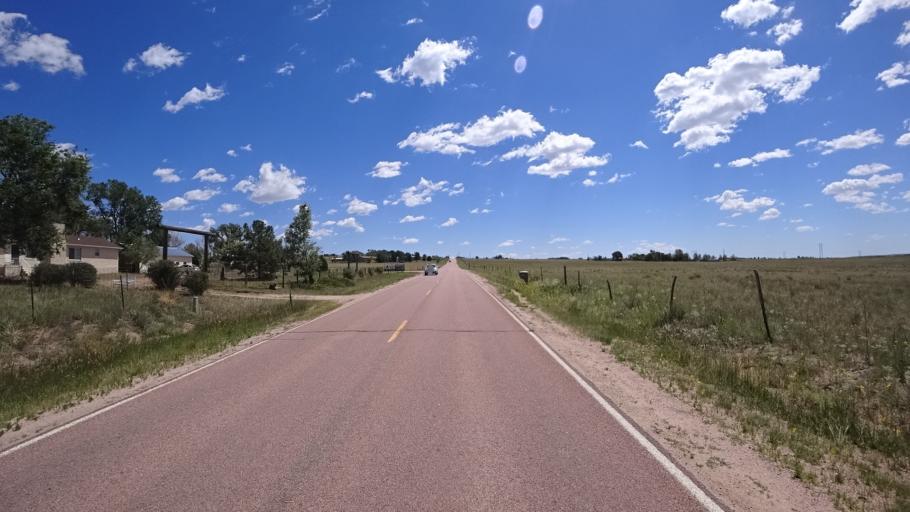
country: US
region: Colorado
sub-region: El Paso County
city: Cimarron Hills
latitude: 38.9115
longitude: -104.6233
